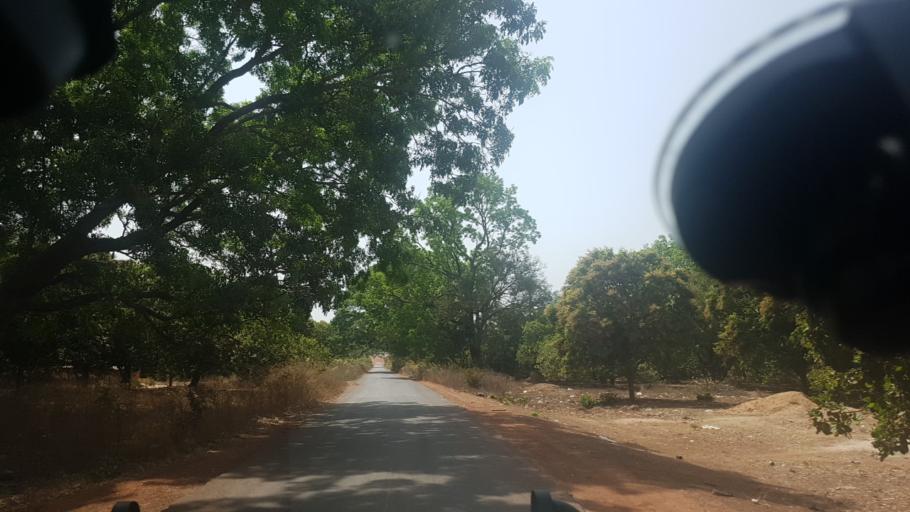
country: GW
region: Cacheu
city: Cacheu
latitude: 12.4130
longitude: -16.0754
